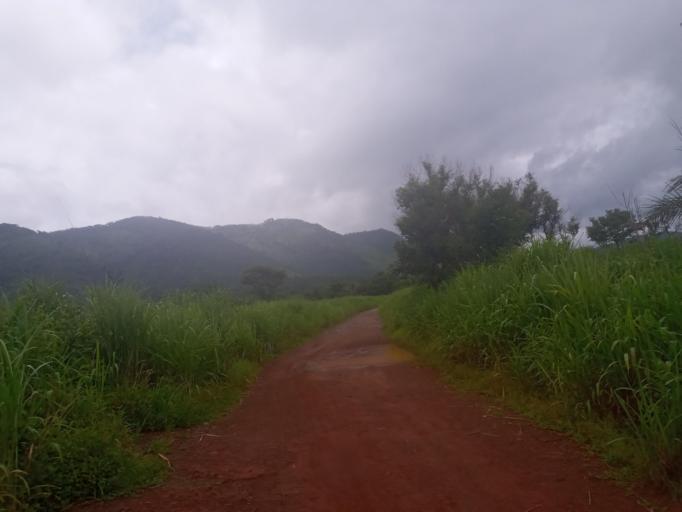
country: SL
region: Northern Province
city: Bumbuna
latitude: 8.9479
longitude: -11.7537
